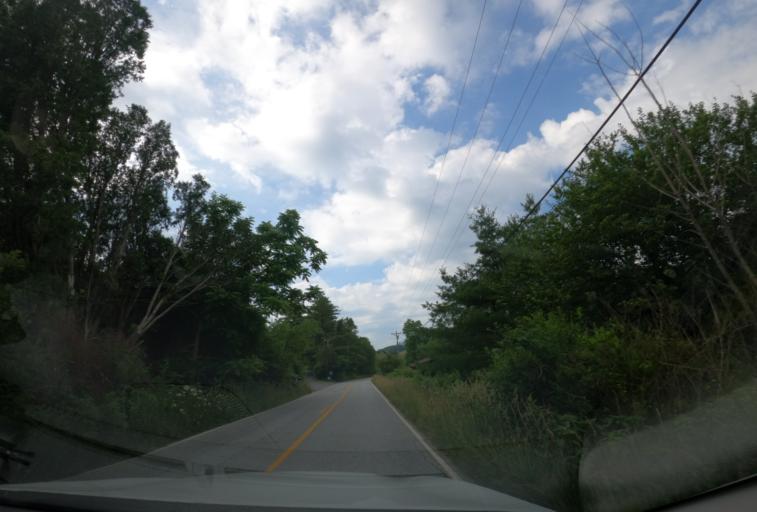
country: US
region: Georgia
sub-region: Rabun County
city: Mountain City
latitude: 35.0069
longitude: -83.3031
